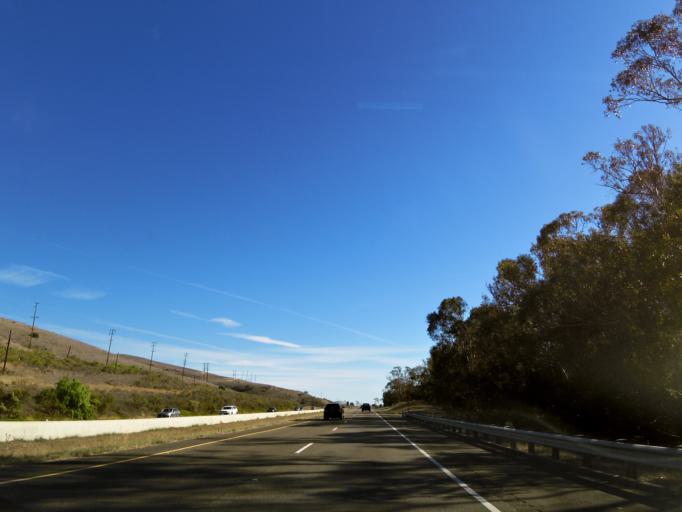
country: US
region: California
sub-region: Santa Barbara County
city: Solvang
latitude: 34.4666
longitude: -120.1063
